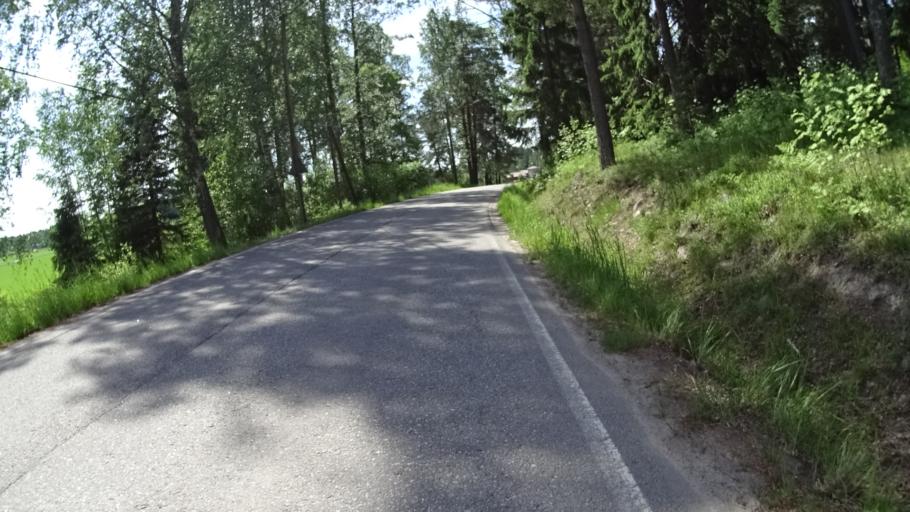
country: FI
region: Uusimaa
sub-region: Helsinki
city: Espoo
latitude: 60.2830
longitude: 24.6755
